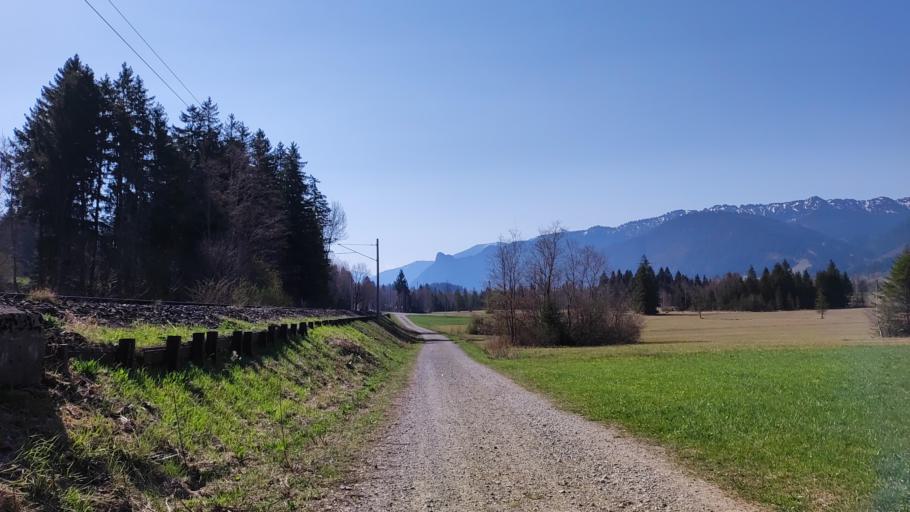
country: DE
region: Bavaria
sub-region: Upper Bavaria
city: Unterammergau
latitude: 47.6399
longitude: 11.0250
